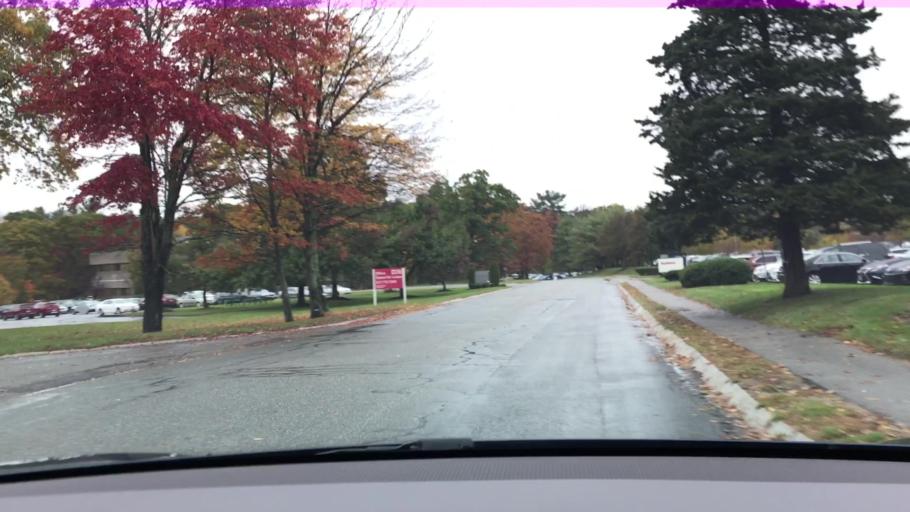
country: US
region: Massachusetts
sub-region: Middlesex County
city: Billerica
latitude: 42.5300
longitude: -71.2807
